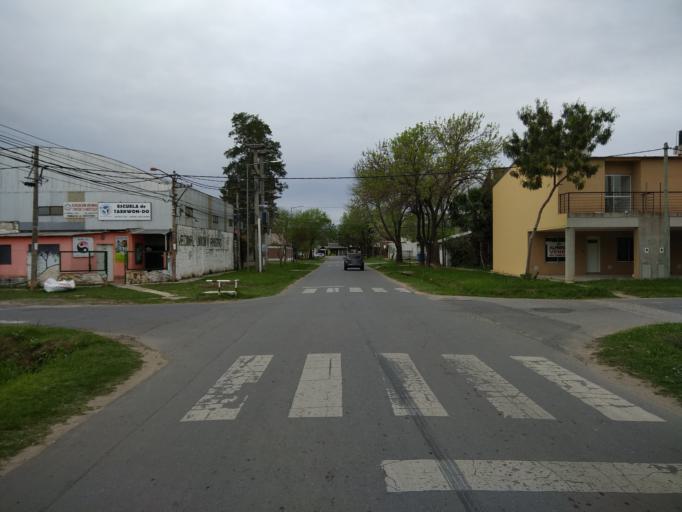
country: AR
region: Santa Fe
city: Granadero Baigorria
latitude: -32.8487
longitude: -60.7019
